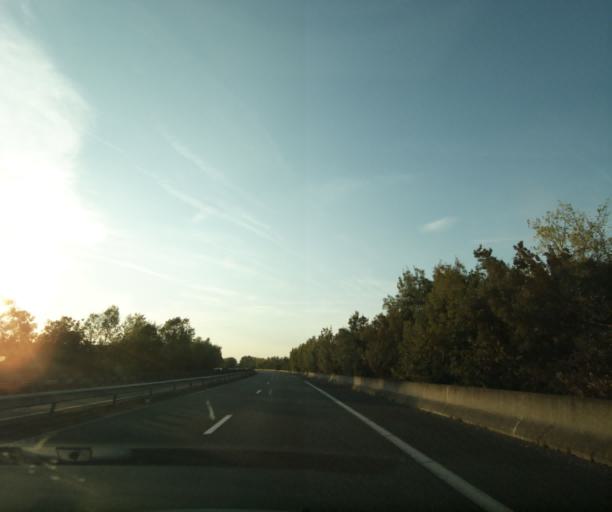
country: FR
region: Aquitaine
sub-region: Departement du Lot-et-Garonne
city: Layrac
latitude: 44.1406
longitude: 0.6671
